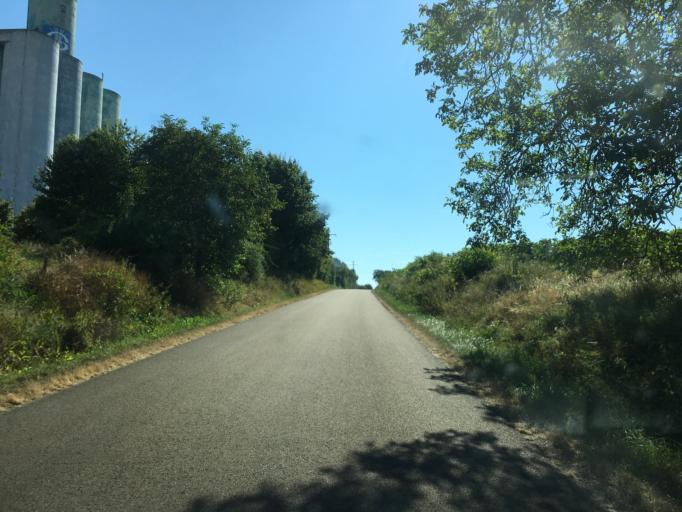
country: FR
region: Bourgogne
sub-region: Departement de l'Yonne
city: Fleury-la-Vallee
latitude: 47.9140
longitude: 3.4264
